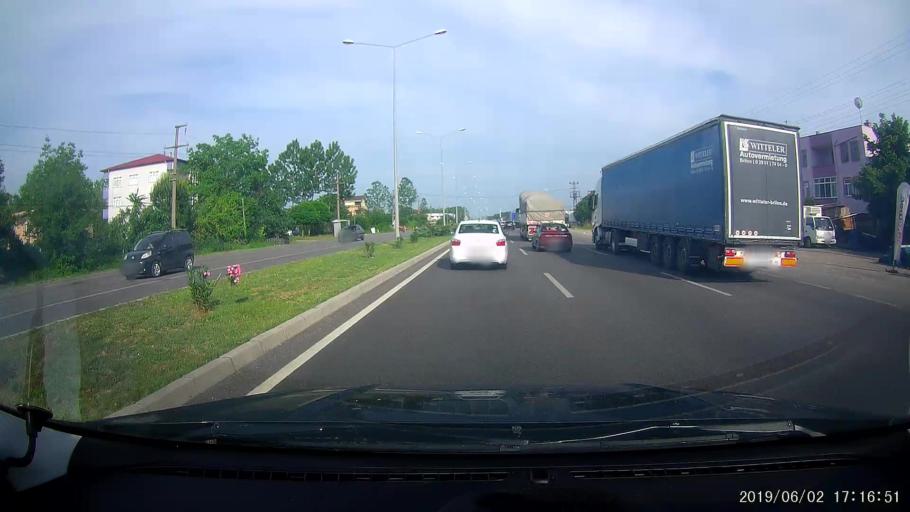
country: TR
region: Samsun
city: Dikbiyik
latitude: 41.2325
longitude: 36.5727
